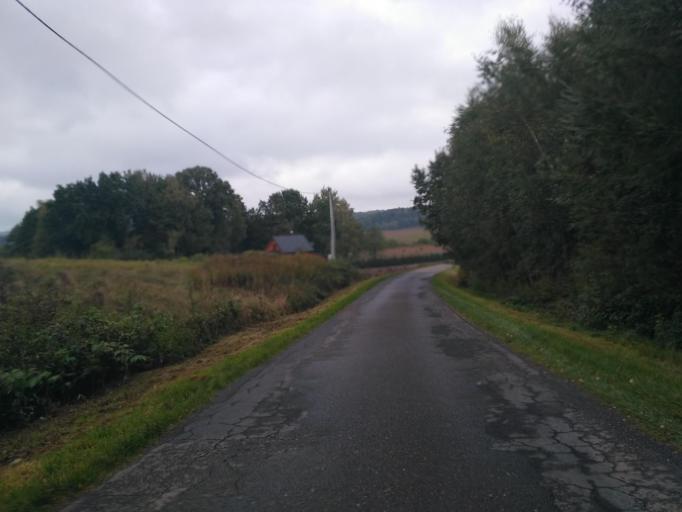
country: PL
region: Subcarpathian Voivodeship
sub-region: Powiat debicki
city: Brzostek
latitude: 49.9343
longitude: 21.4466
